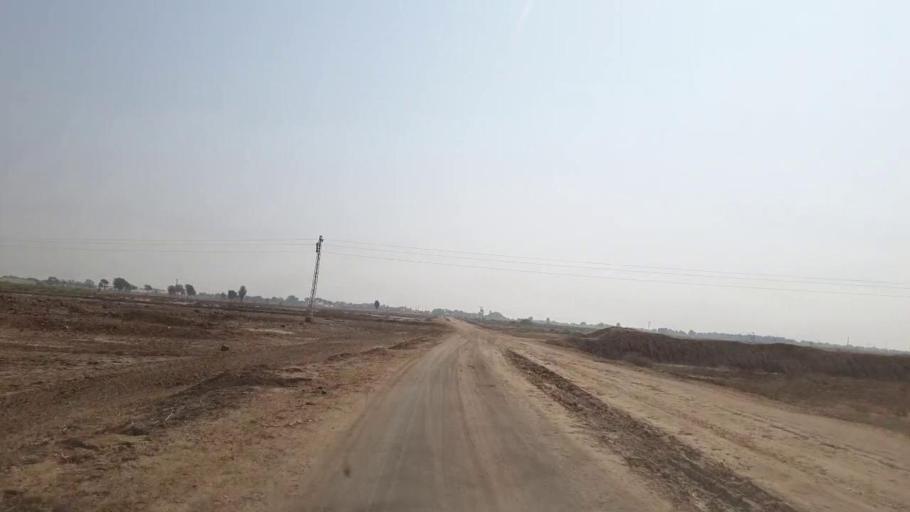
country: PK
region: Sindh
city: Mirpur Khas
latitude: 25.6449
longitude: 69.1412
